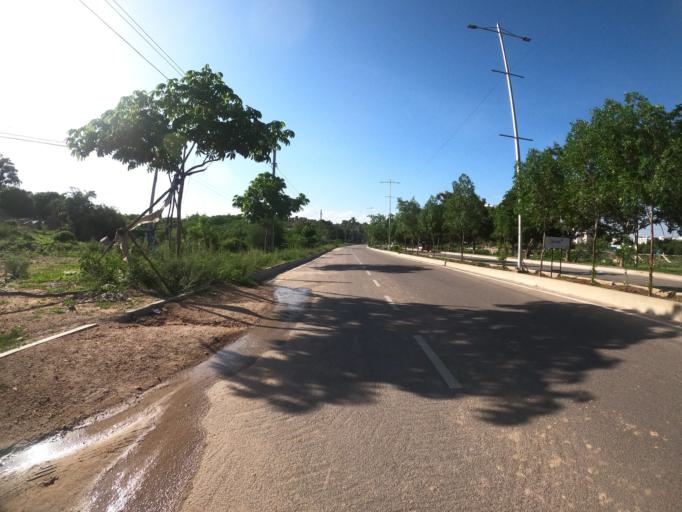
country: IN
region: Telangana
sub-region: Hyderabad
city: Hyderabad
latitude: 17.3553
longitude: 78.3697
